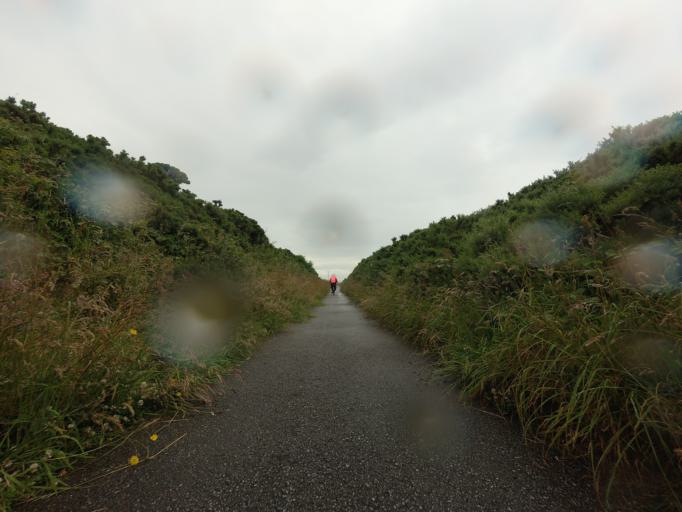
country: GB
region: Scotland
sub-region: Moray
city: Findochty
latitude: 57.6921
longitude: -2.9111
